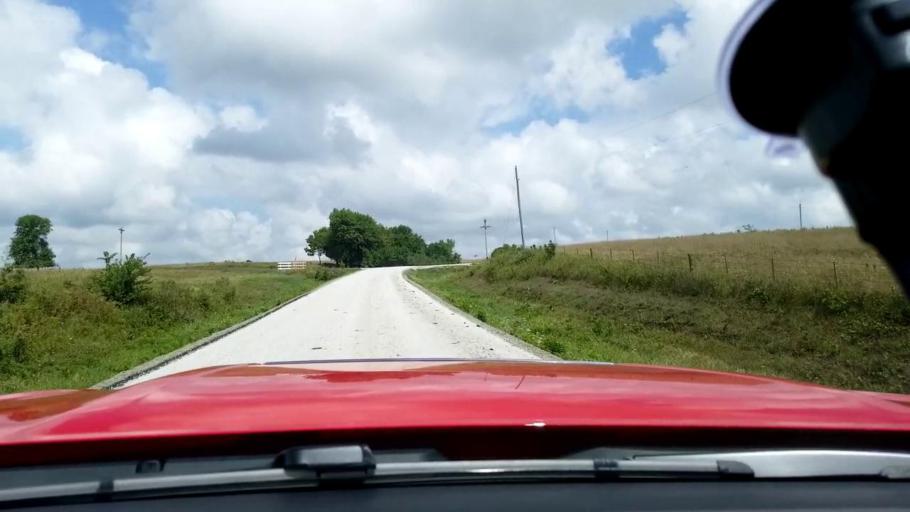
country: US
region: Iowa
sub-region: Decatur County
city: Lamoni
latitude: 40.6518
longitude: -94.0530
